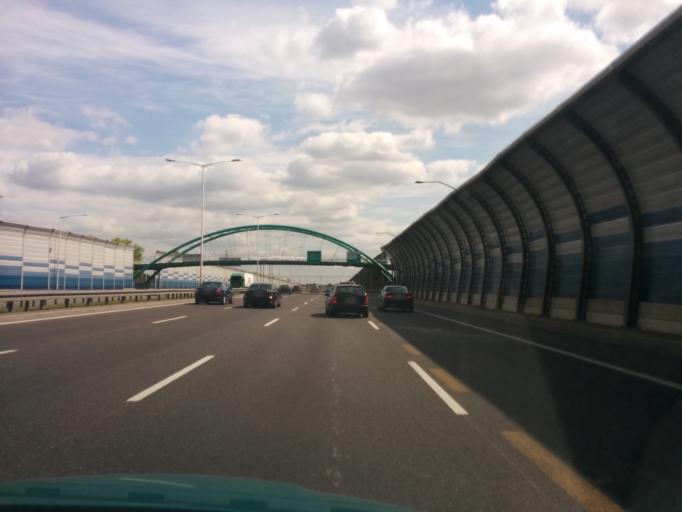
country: PL
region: Masovian Voivodeship
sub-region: Warszawa
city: Targowek
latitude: 52.3015
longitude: 21.0402
